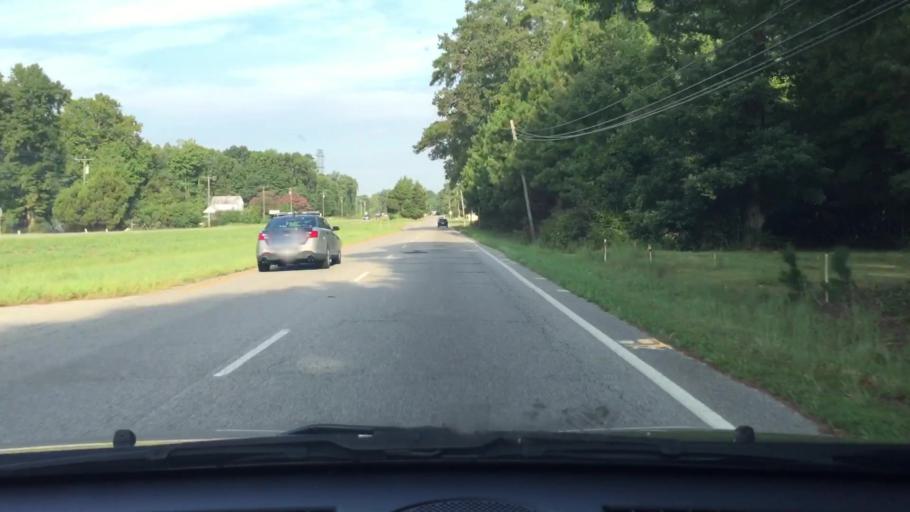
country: US
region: Virginia
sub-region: Isle of Wight County
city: Carrollton
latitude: 36.9412
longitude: -76.5440
